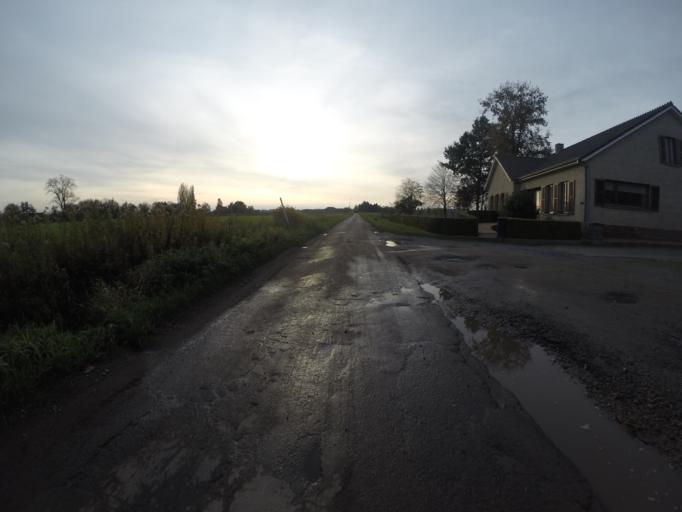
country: BE
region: Flanders
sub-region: Provincie Oost-Vlaanderen
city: Aalter
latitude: 51.0601
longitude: 3.4852
